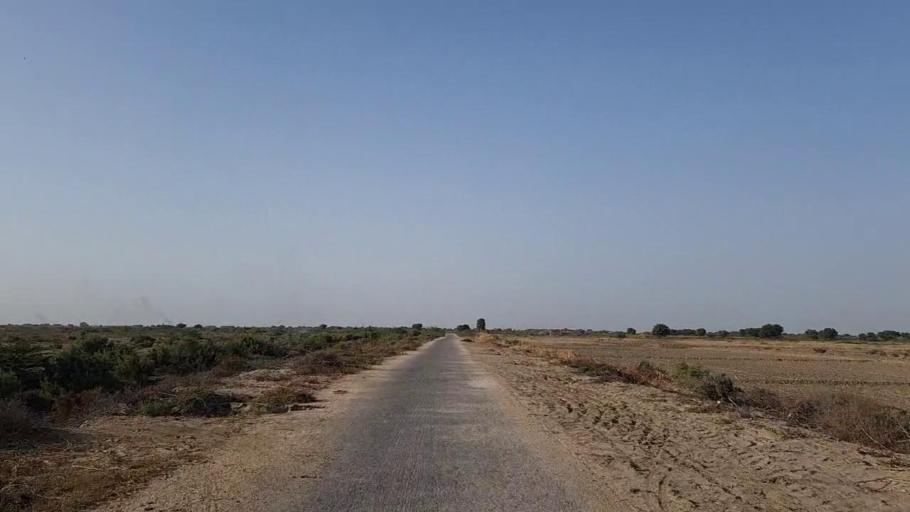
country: PK
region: Sindh
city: Jati
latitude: 24.3010
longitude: 68.1691
